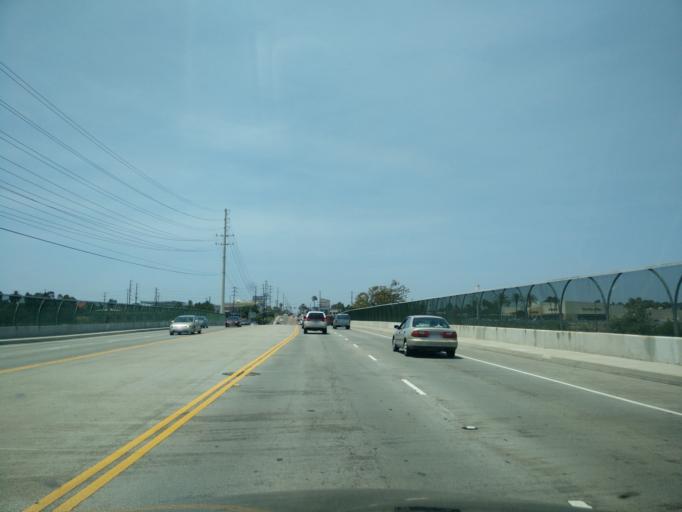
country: US
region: California
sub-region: San Diego County
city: Chula Vista
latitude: 32.6551
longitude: -117.0897
